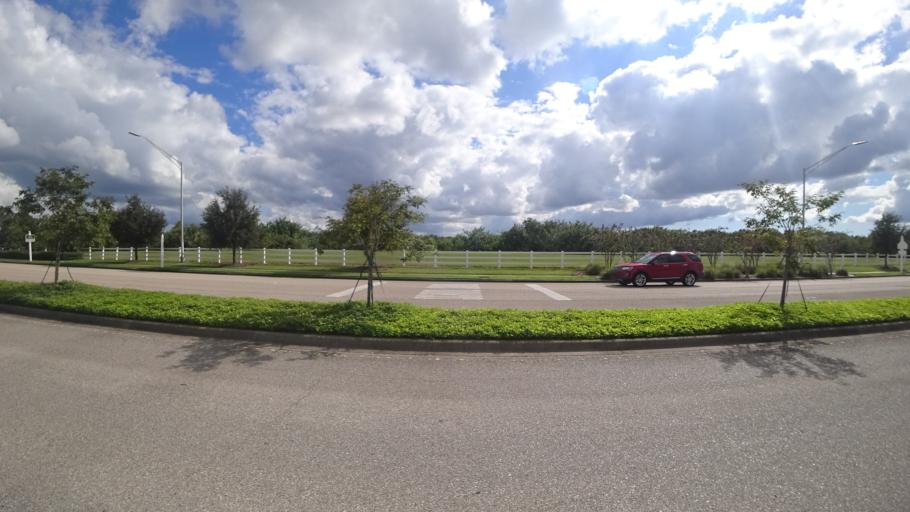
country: US
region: Florida
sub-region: Sarasota County
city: The Meadows
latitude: 27.3967
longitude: -82.3950
